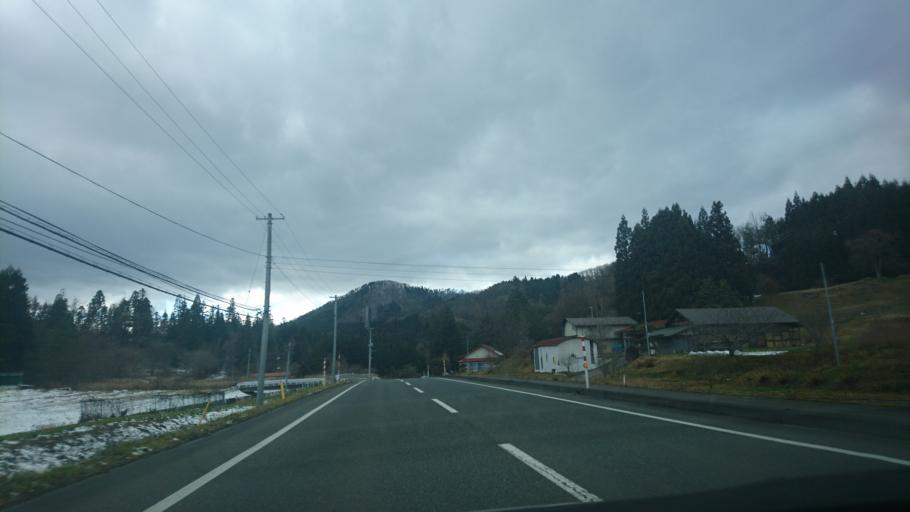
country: JP
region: Iwate
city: Mizusawa
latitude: 39.1812
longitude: 141.2976
